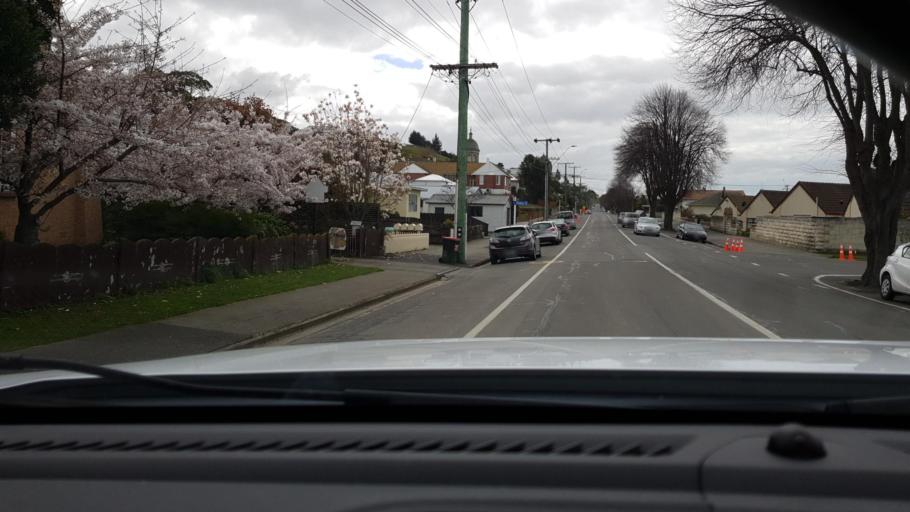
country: NZ
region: Otago
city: Oamaru
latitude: -45.0952
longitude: 170.9688
